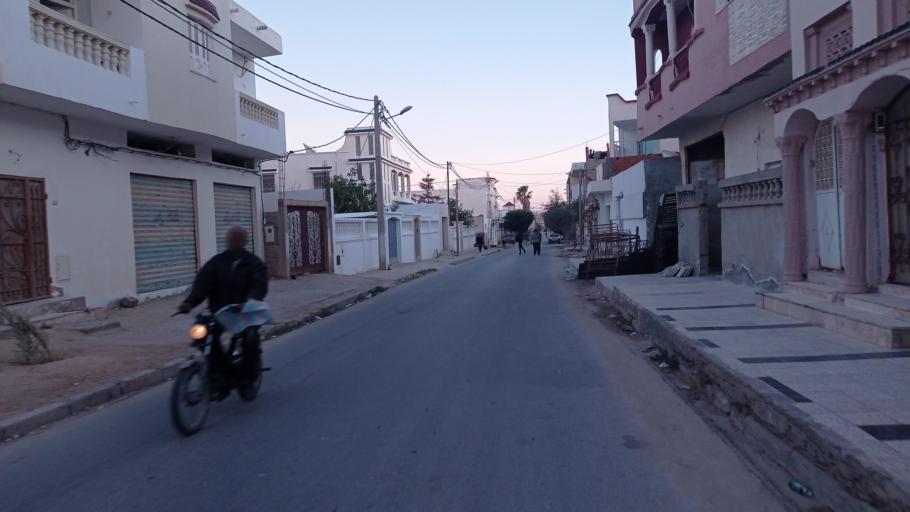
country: TN
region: Qabis
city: Gabes
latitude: 33.8475
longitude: 10.1137
